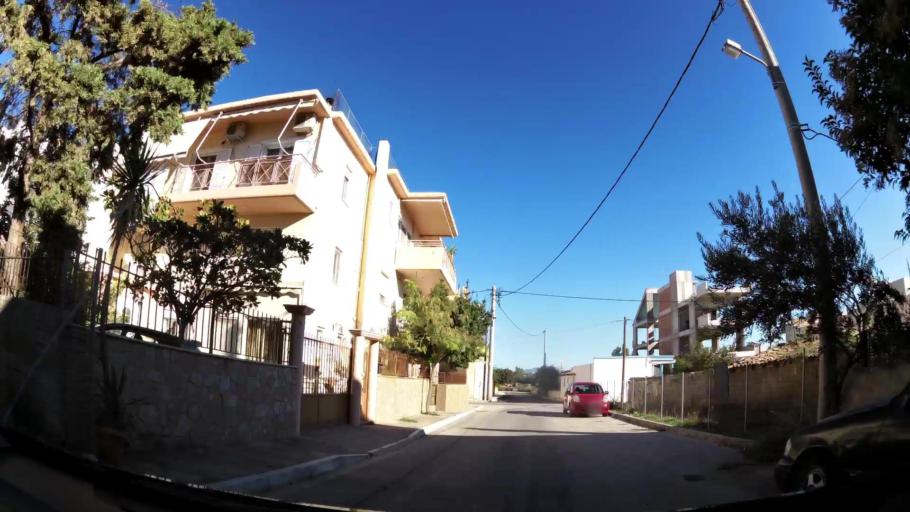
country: GR
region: Attica
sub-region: Nomarchia Anatolikis Attikis
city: Koropi
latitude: 37.9033
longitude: 23.8669
